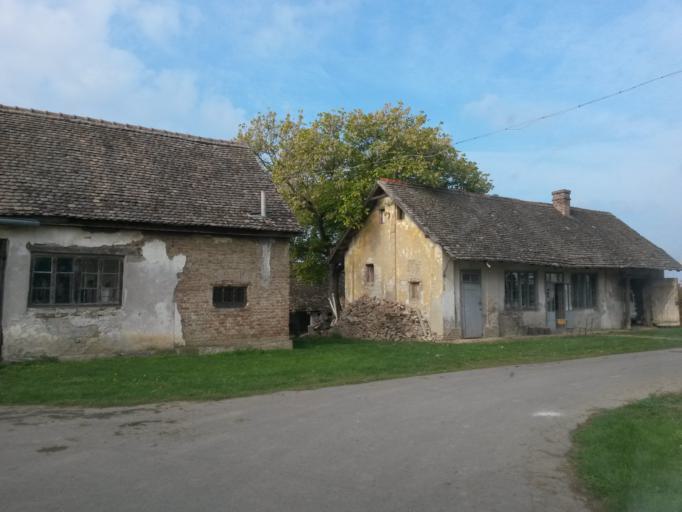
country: HR
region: Vukovarsko-Srijemska
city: Ilok
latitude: 45.2145
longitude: 19.3815
